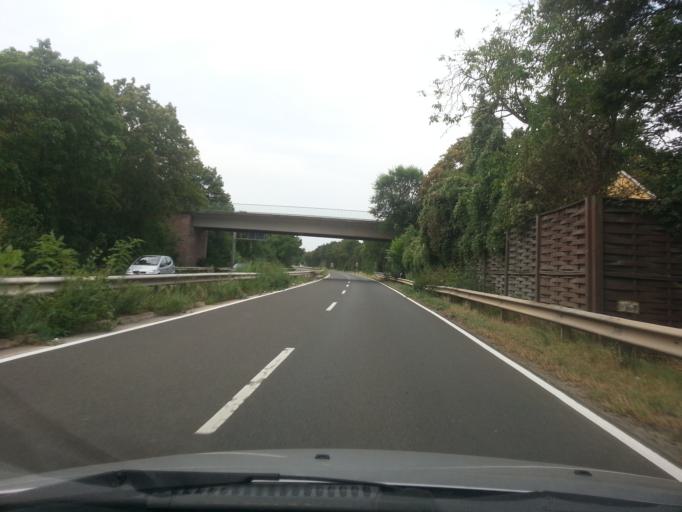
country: DE
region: Rheinland-Pfalz
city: Worms
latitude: 49.6195
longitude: 8.3617
